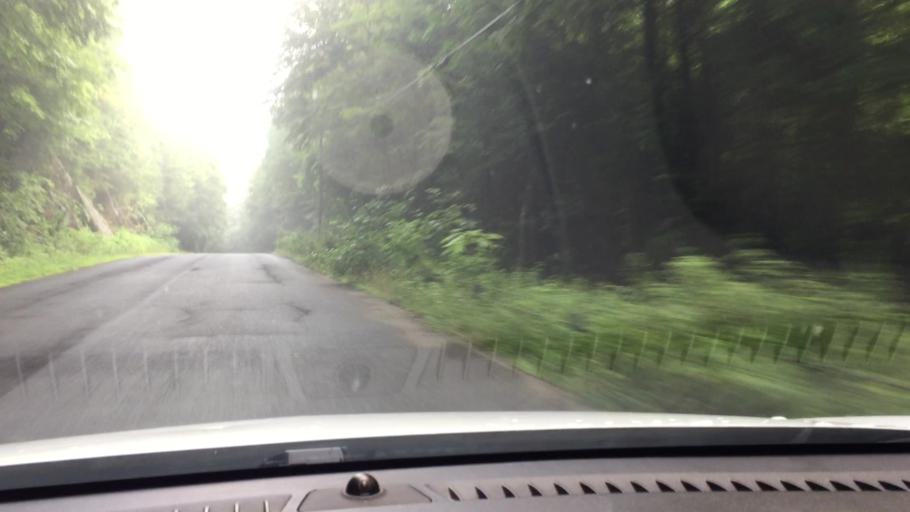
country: US
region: Massachusetts
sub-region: Hampshire County
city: Chesterfield
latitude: 42.2957
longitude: -72.9049
